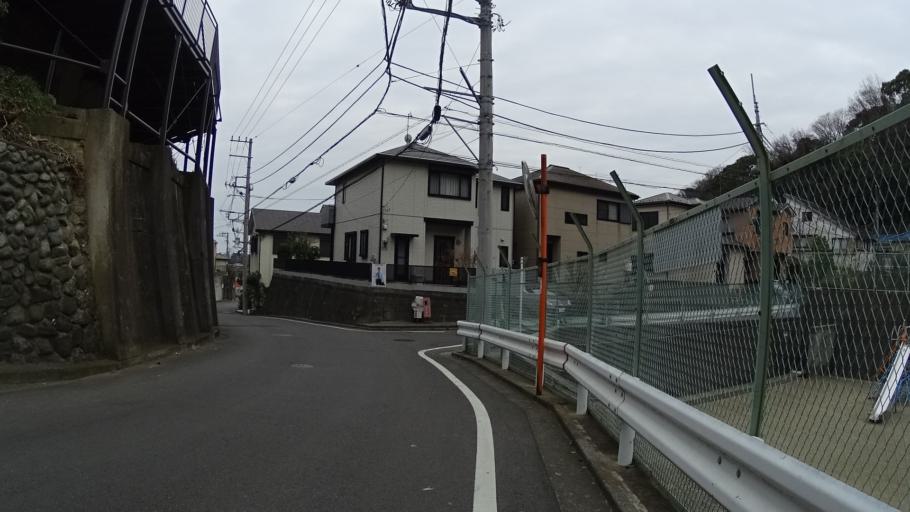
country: JP
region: Kanagawa
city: Oiso
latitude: 35.3144
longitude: 139.3074
